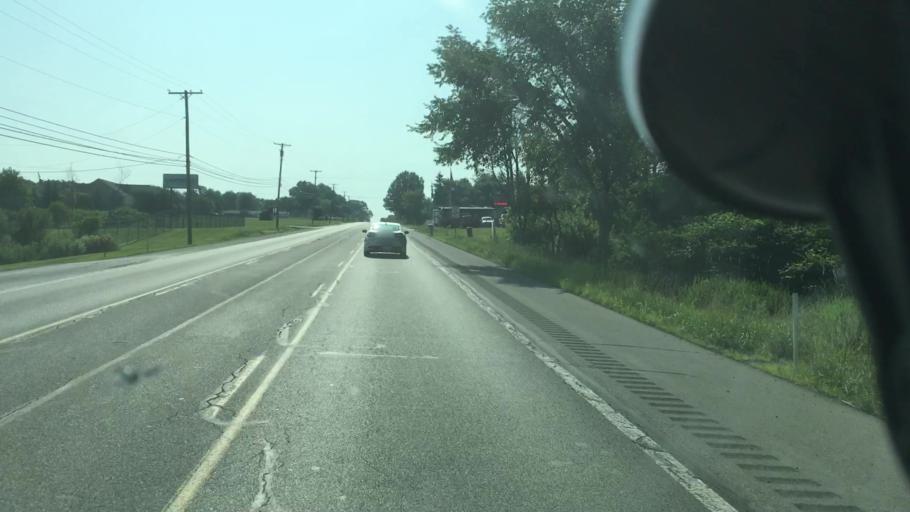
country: US
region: Pennsylvania
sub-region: Lawrence County
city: New Castle
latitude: 40.9762
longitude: -80.2855
